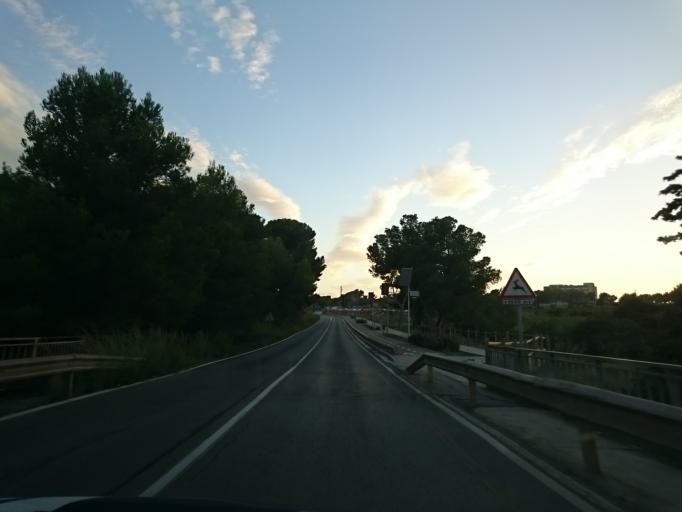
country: ES
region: Catalonia
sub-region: Provincia de Barcelona
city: Sant Pere de Ribes
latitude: 41.2555
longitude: 1.7708
